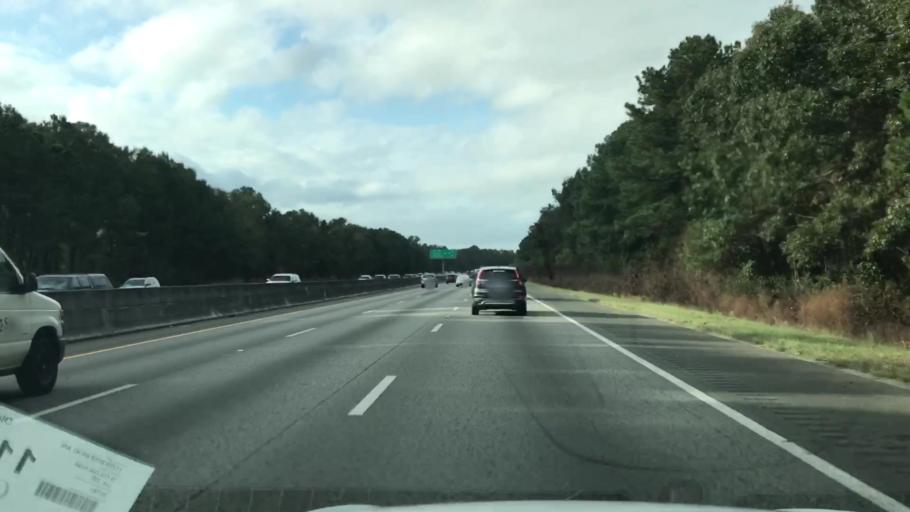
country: US
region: South Carolina
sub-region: Berkeley County
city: Goose Creek
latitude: 32.9573
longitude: -80.0674
